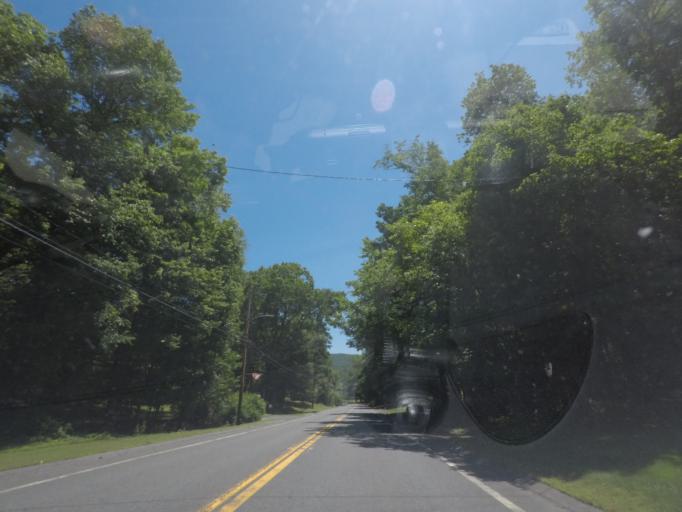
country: US
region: Massachusetts
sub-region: Berkshire County
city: Becket
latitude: 42.2703
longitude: -72.9678
